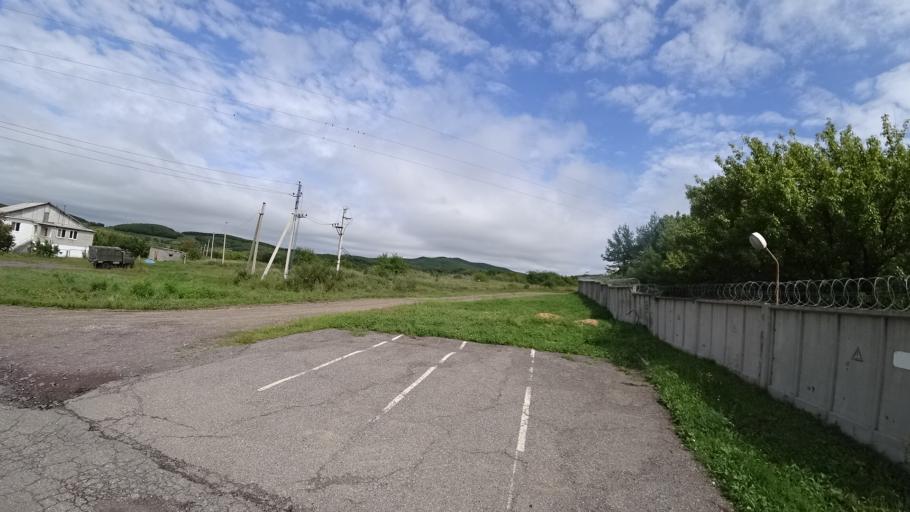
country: RU
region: Primorskiy
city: Lyalichi
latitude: 44.1300
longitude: 132.3888
